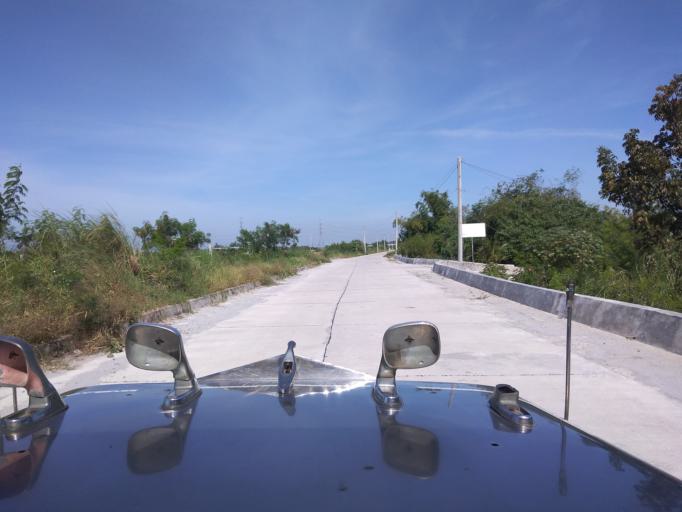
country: PH
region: Central Luzon
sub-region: Province of Pampanga
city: Bacolor
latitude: 15.0023
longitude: 120.6609
